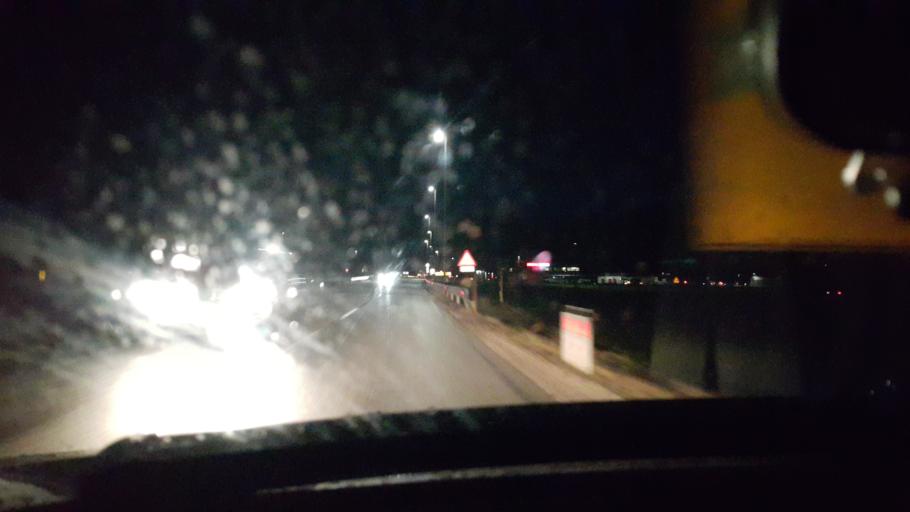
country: SI
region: Polzela
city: Polzela
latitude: 46.2613
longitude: 15.0703
